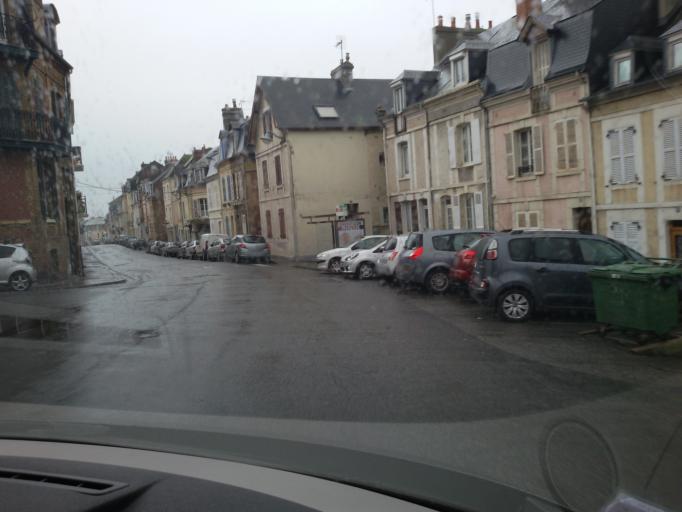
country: FR
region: Lower Normandy
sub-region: Departement du Calvados
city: Trouville-sur-Mer
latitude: 49.3649
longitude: 0.0840
